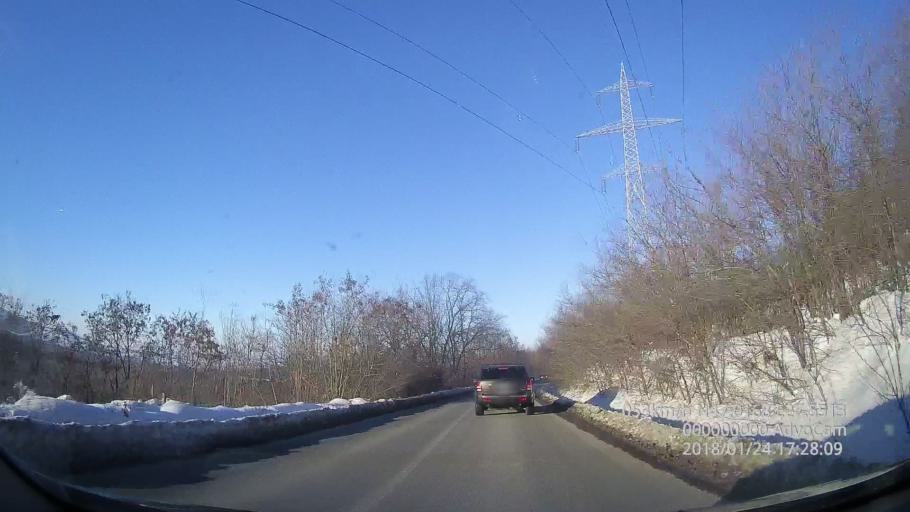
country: RO
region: Iasi
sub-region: Comuna Mogosesti
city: Mogosesti
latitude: 47.0173
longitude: 27.5513
